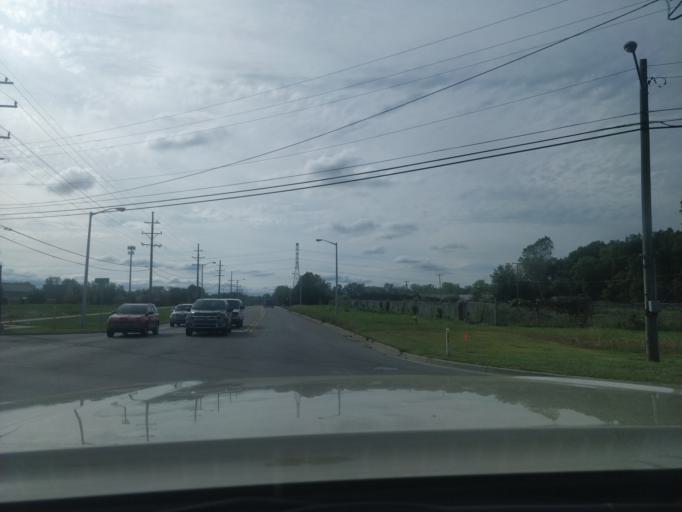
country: US
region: Michigan
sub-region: Wayne County
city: Woodhaven
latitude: 42.1539
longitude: -83.2532
